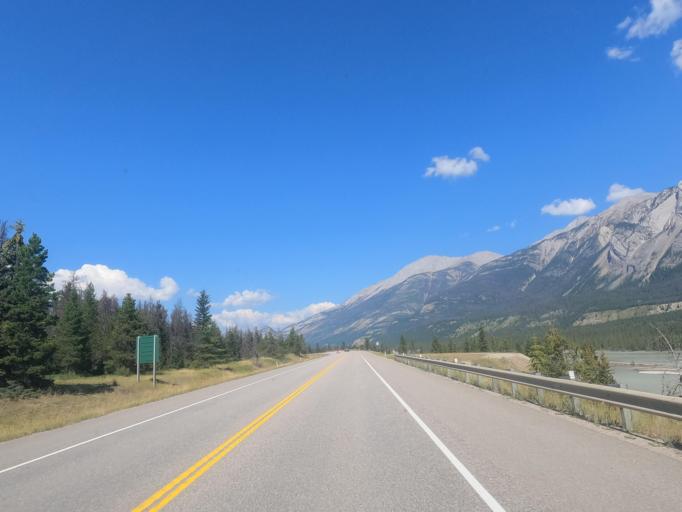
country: CA
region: Alberta
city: Jasper Park Lodge
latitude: 52.9452
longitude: -118.0394
